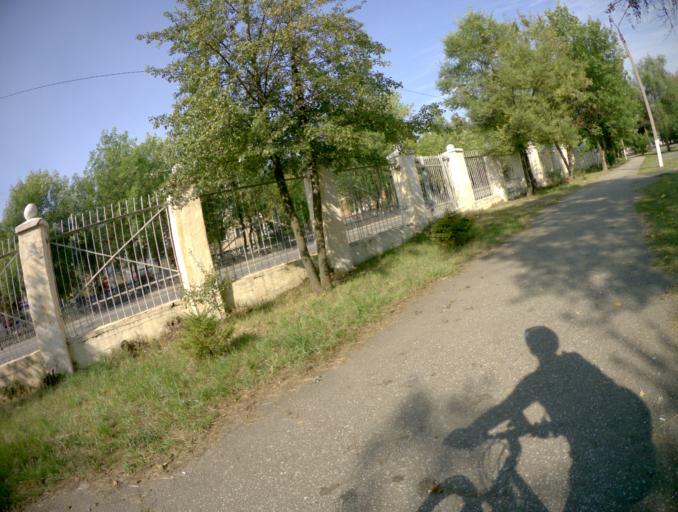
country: RU
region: Vladimir
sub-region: Kovrovskiy Rayon
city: Kovrov
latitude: 56.3728
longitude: 41.3060
